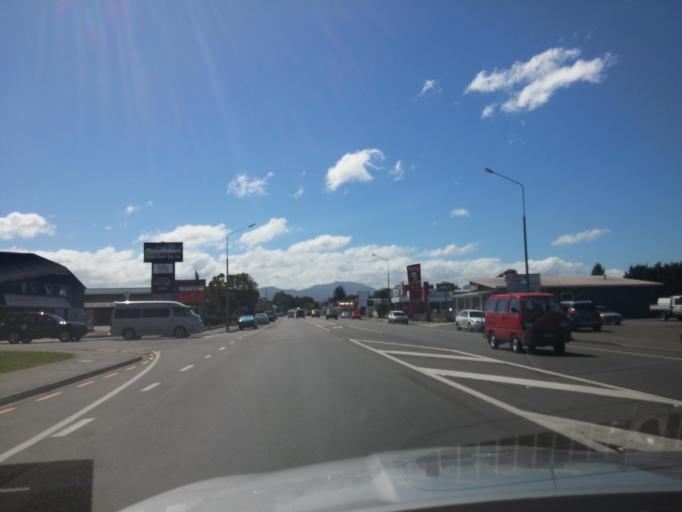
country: NZ
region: Marlborough
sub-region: Marlborough District
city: Blenheim
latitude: -41.5049
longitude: 173.9601
